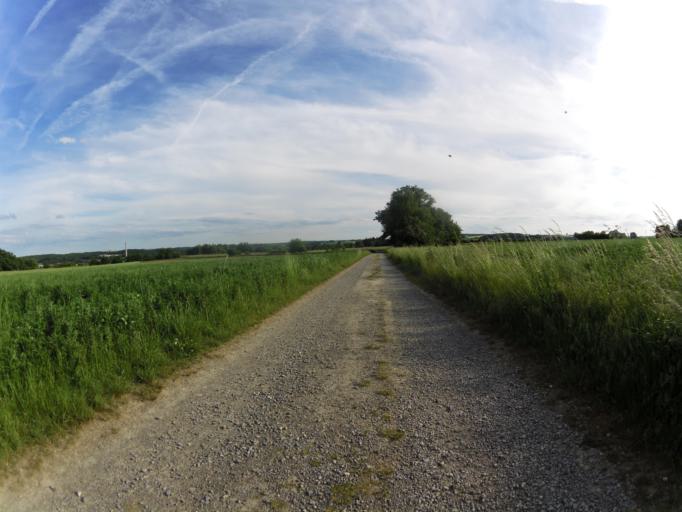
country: DE
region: Bavaria
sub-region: Regierungsbezirk Unterfranken
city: Ochsenfurt
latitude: 49.6764
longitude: 10.0712
